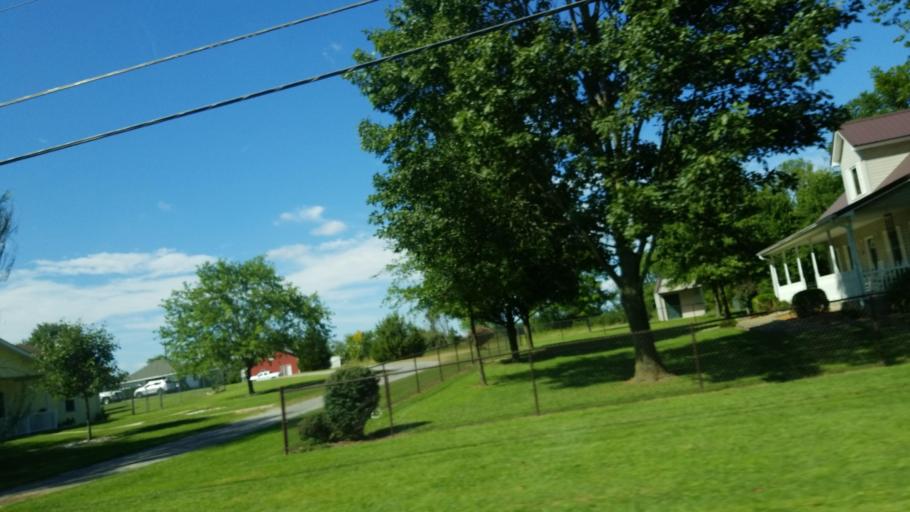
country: US
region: Illinois
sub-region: Williamson County
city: Marion
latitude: 37.7409
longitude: -88.9089
